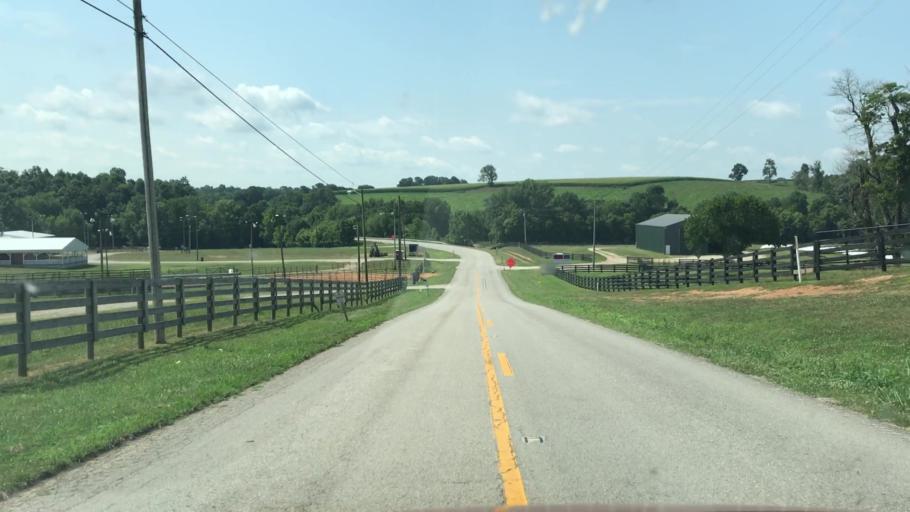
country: US
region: Kentucky
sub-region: Barren County
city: Glasgow
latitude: 36.8688
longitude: -85.8487
